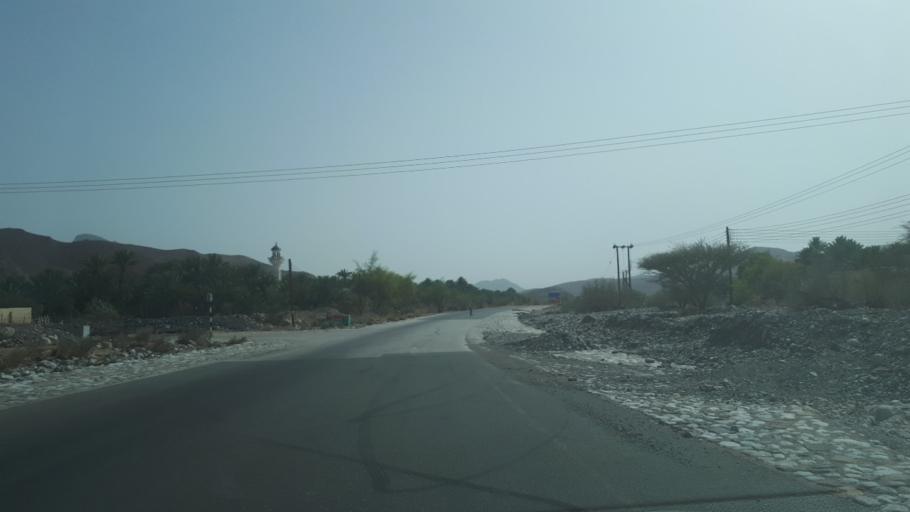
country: OM
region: Muhafazat ad Dakhiliyah
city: Bahla'
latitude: 23.2126
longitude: 56.9628
